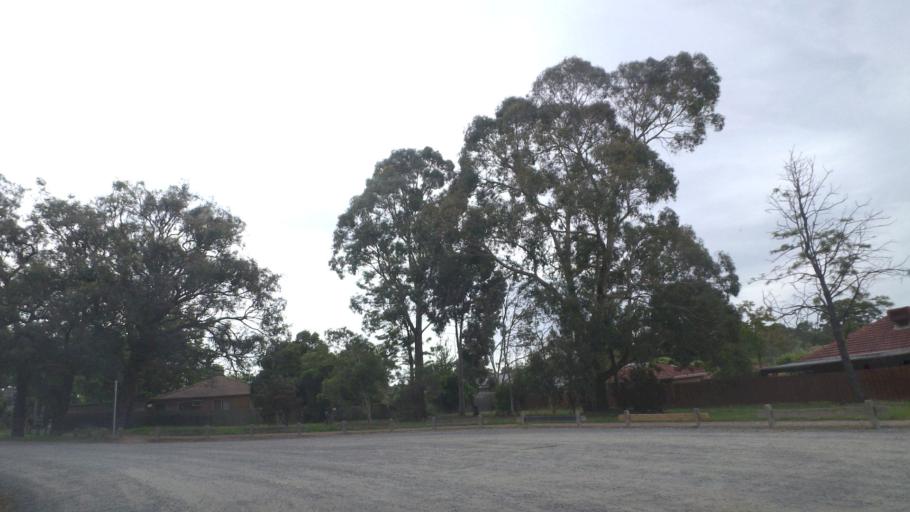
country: AU
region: Victoria
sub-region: Maroondah
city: Croydon South
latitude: -37.7967
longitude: 145.2645
